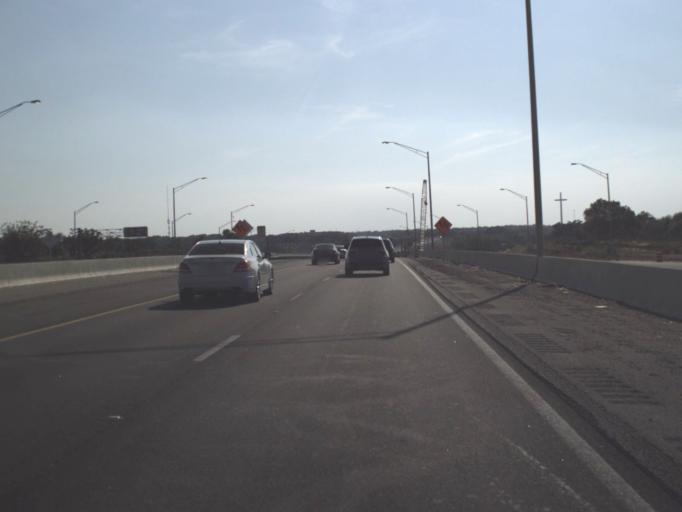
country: US
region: Florida
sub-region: Orange County
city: Orlovista
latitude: 28.5481
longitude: -81.4924
